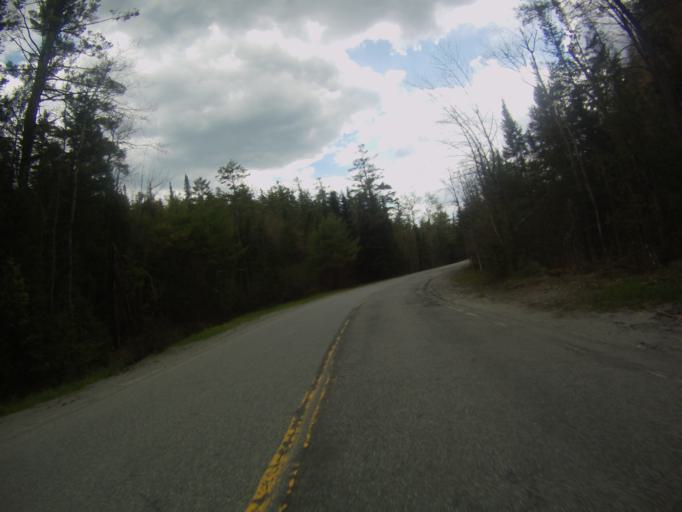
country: US
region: New York
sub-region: Essex County
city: Mineville
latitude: 44.0763
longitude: -73.6265
